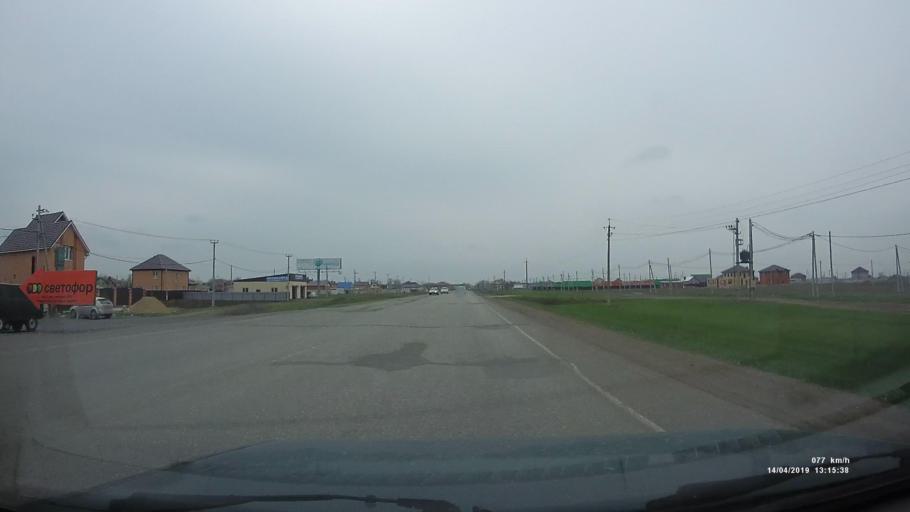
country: RU
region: Rostov
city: Kuleshovka
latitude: 47.0829
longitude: 39.5922
